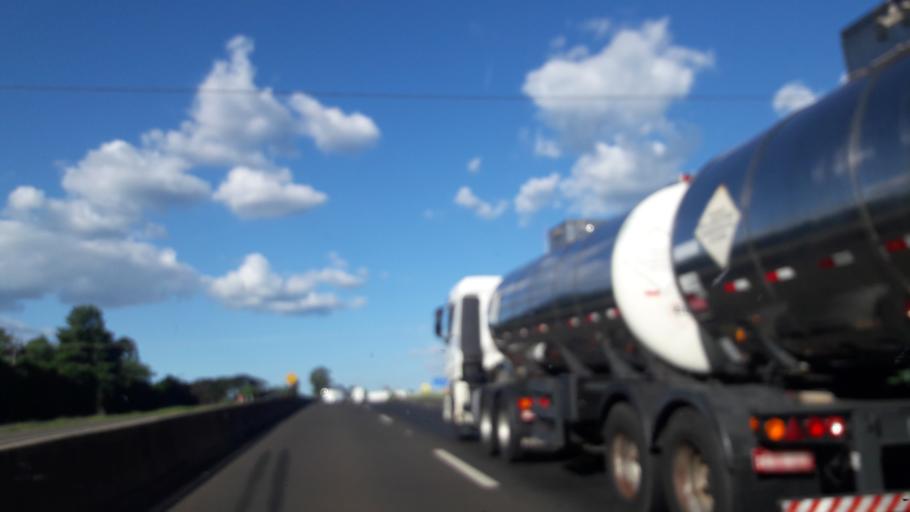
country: BR
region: Parana
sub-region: Guarapuava
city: Guarapuava
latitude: -25.3505
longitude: -51.4569
